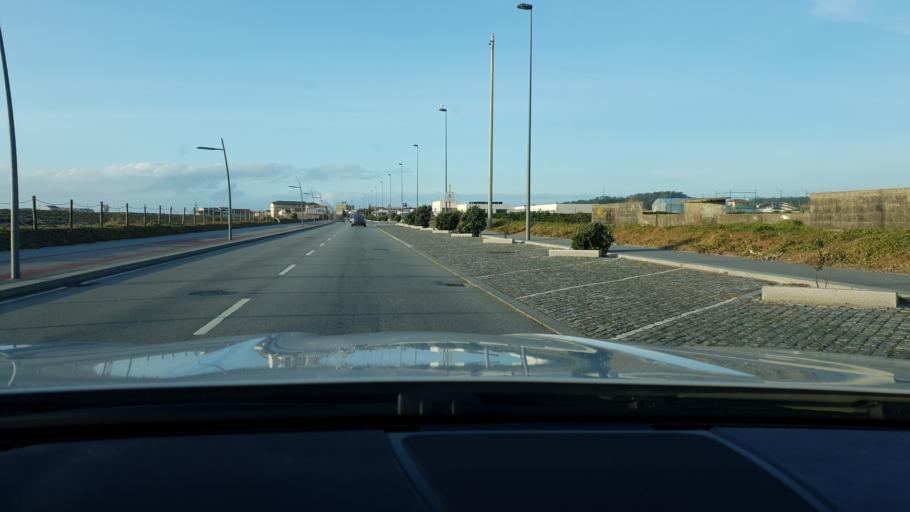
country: PT
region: Porto
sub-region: Matosinhos
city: Lavra
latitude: 41.2314
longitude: -8.7196
